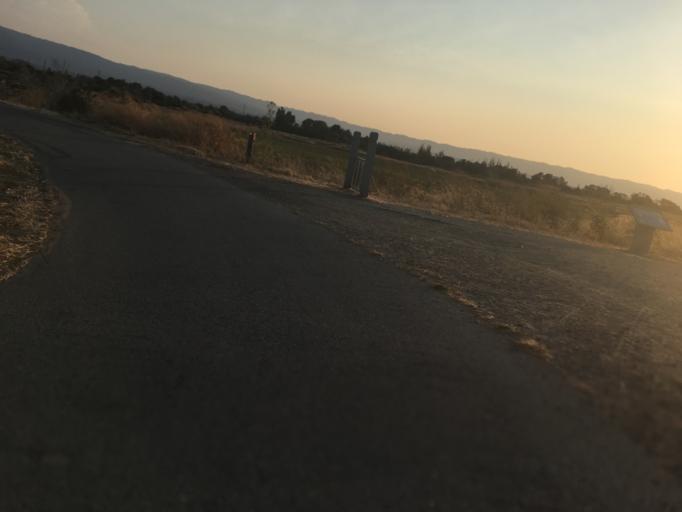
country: US
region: California
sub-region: Santa Clara County
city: Mountain View
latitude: 37.4349
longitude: -122.0815
